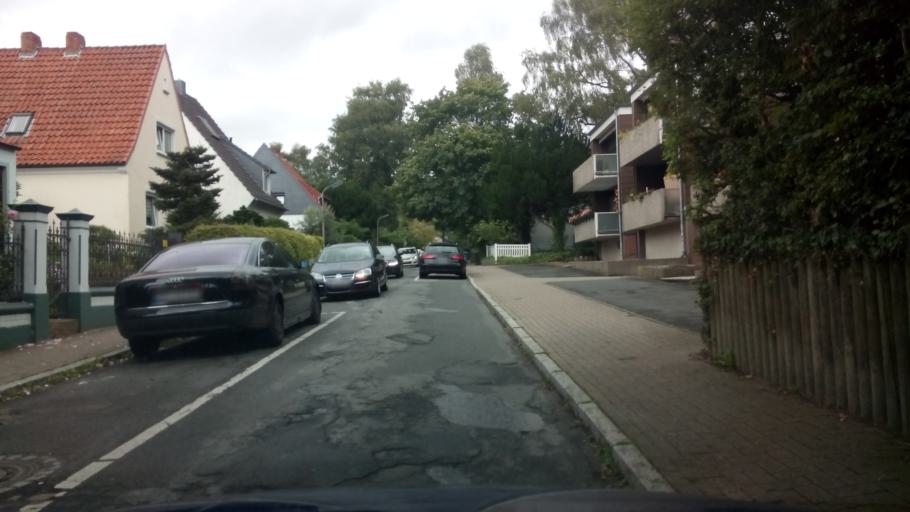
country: DE
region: Lower Saxony
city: Lemwerder
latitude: 53.1729
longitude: 8.6279
